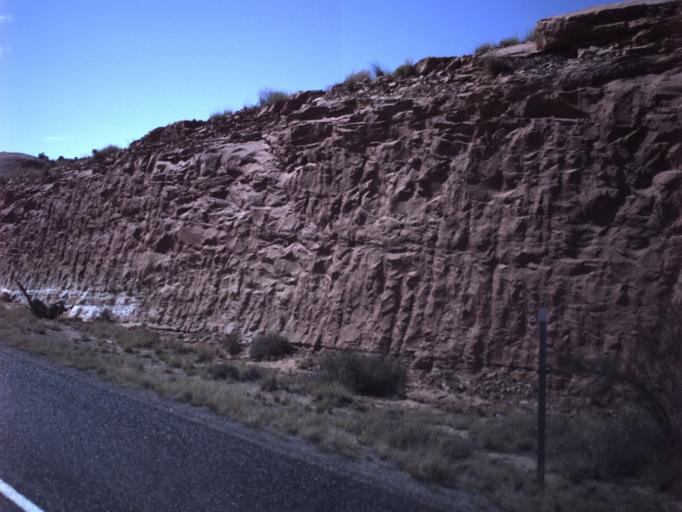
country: US
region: Utah
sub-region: Grand County
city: Moab
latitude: 38.6454
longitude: -109.7351
